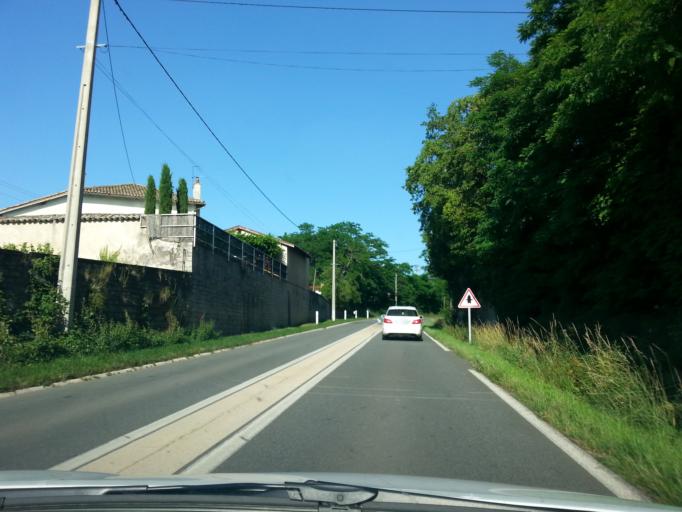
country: FR
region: Rhone-Alpes
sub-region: Departement du Rhone
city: Charentay
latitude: 46.1202
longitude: 4.6867
